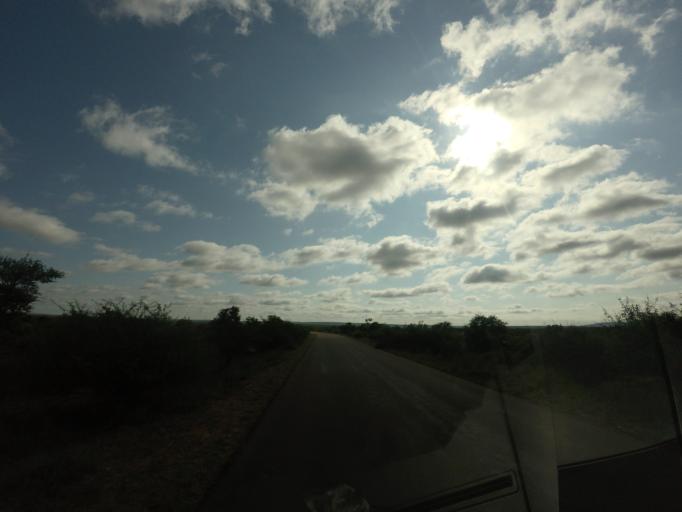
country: ZA
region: Mpumalanga
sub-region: Ehlanzeni District
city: Komatipoort
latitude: -25.1651
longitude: 31.9274
